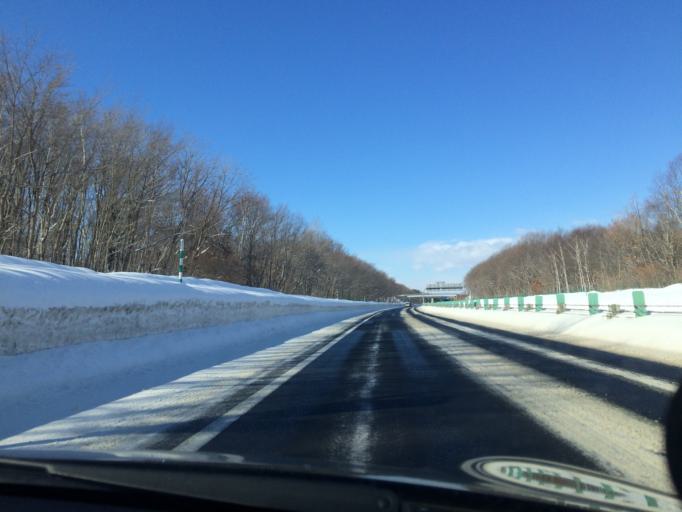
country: JP
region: Hokkaido
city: Chitose
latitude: 42.8490
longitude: 141.5741
